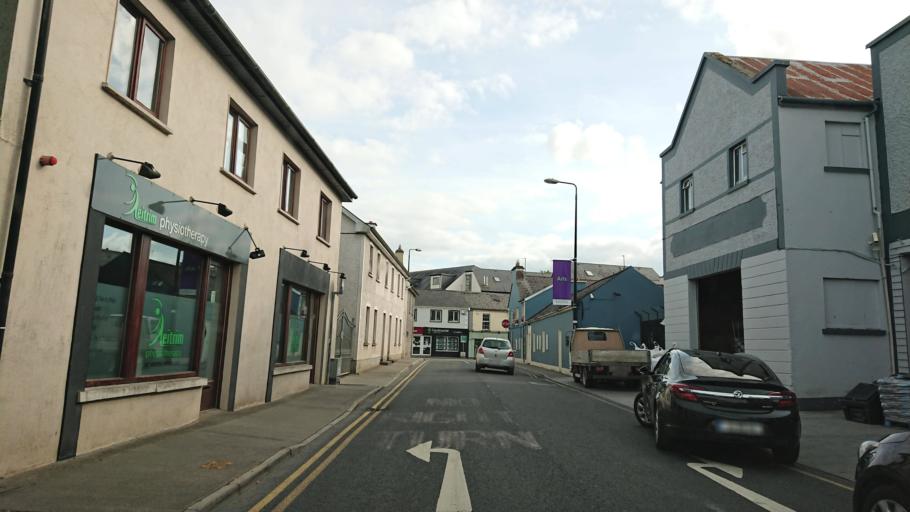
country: IE
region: Connaught
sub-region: County Leitrim
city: Carrick-on-Shannon
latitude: 53.9475
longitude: -8.0918
